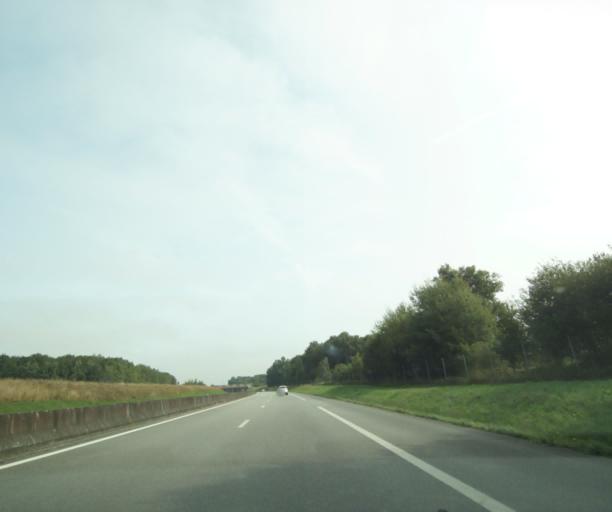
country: FR
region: Lower Normandy
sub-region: Departement de l'Orne
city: Sees
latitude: 48.5467
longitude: 0.1731
